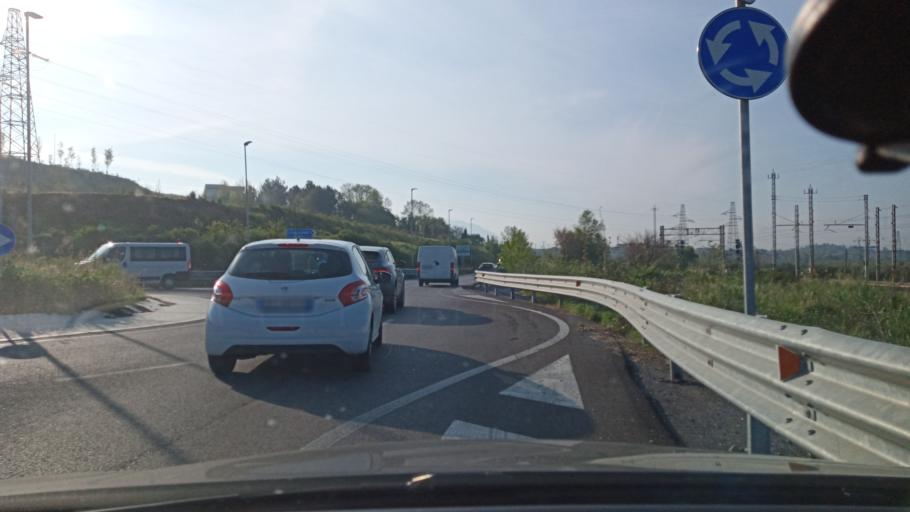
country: IT
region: Latium
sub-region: Citta metropolitana di Roma Capitale
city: Fiano Romano
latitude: 42.1665
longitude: 12.6416
